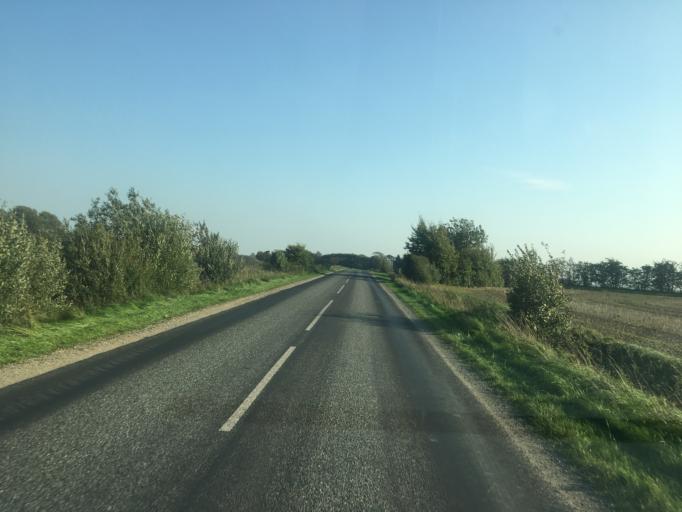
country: DE
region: Schleswig-Holstein
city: Bramstedtlund
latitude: 54.9511
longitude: 9.0575
